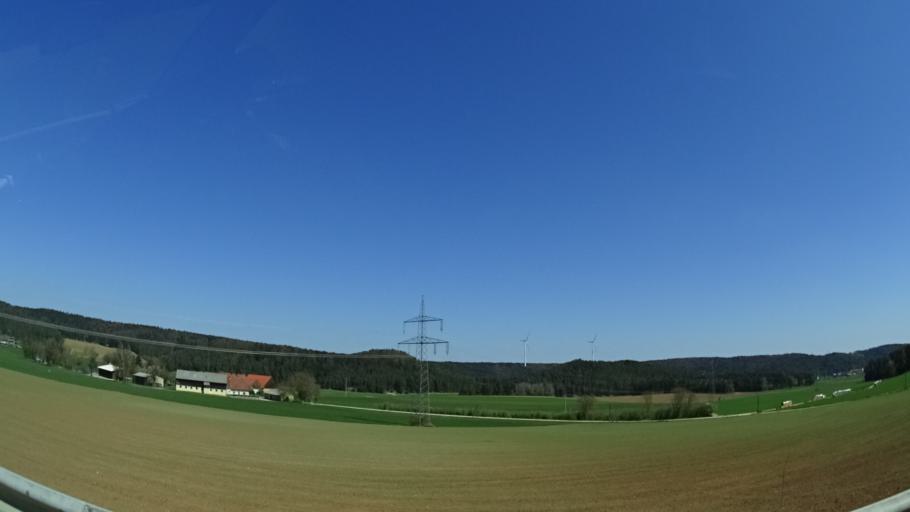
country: DE
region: Bavaria
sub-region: Upper Palatinate
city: Kastl
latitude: 49.4005
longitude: 11.6952
